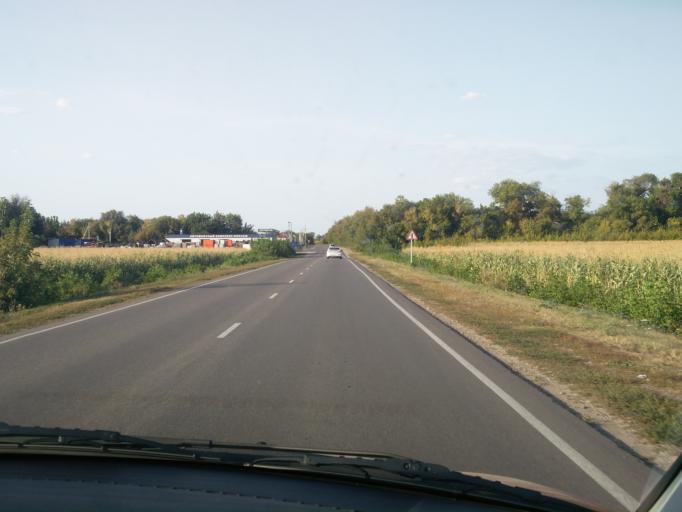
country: RU
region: Voronezj
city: Ramon'
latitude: 51.9158
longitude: 39.3196
